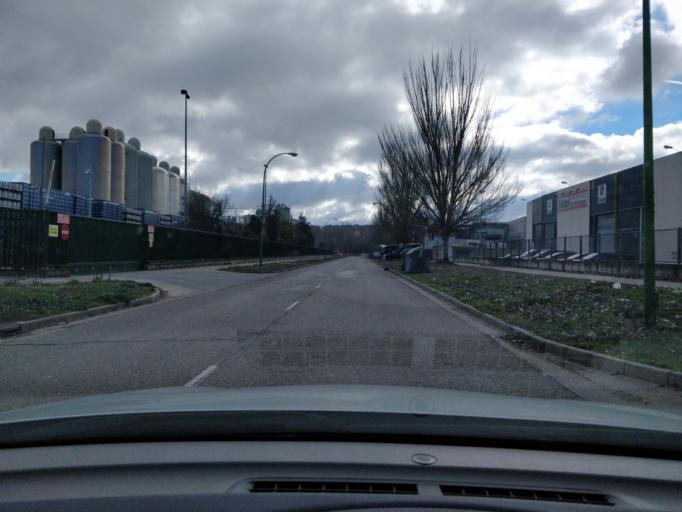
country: ES
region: Castille and Leon
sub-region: Provincia de Burgos
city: Burgos
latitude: 42.3488
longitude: -3.6582
